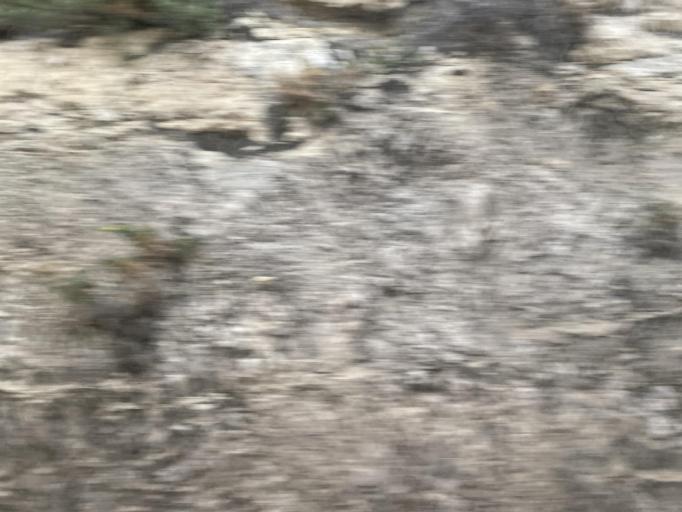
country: ES
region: Catalonia
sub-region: Provincia de Barcelona
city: Vilanova i la Geltru
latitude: 41.2193
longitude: 1.7491
